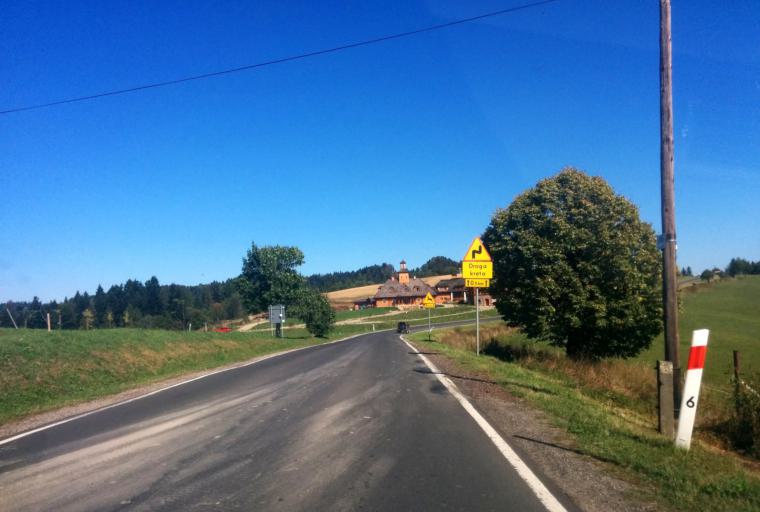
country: PL
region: Subcarpathian Voivodeship
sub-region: Powiat bieszczadzki
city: Lutowiska
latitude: 49.2613
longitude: 22.6831
